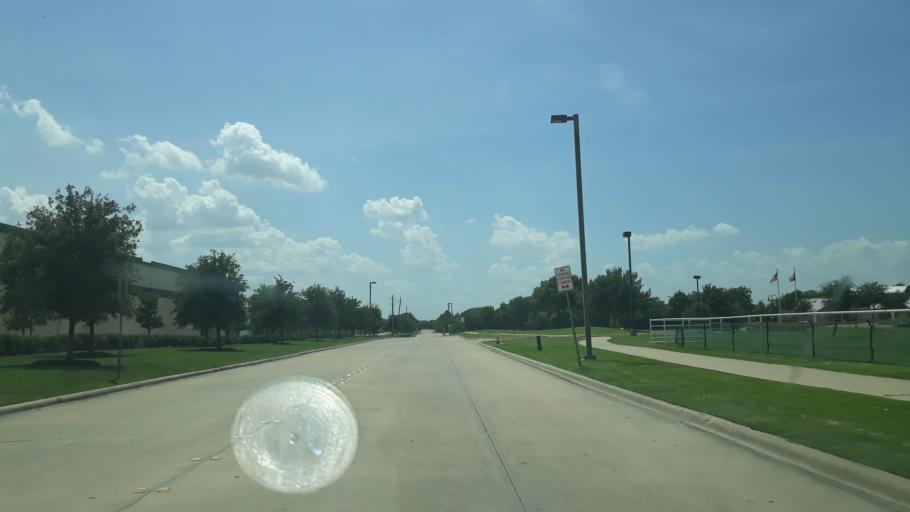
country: US
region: Texas
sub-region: Dallas County
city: Coppell
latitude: 32.9610
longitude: -97.0194
